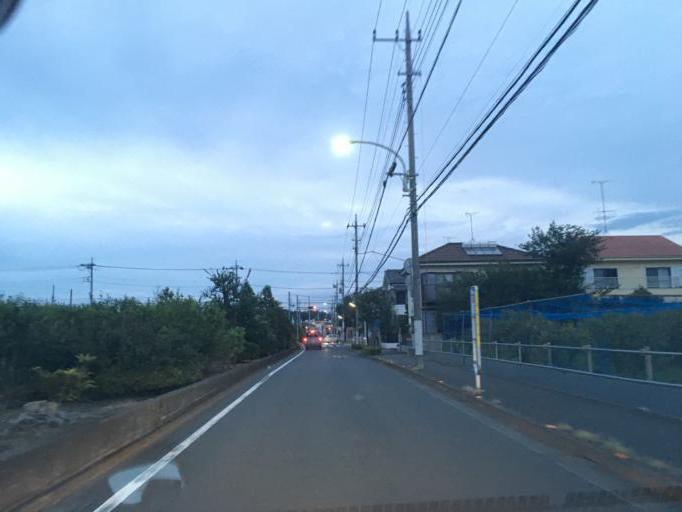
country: JP
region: Tokyo
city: Kokubunji
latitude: 35.7183
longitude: 139.4563
